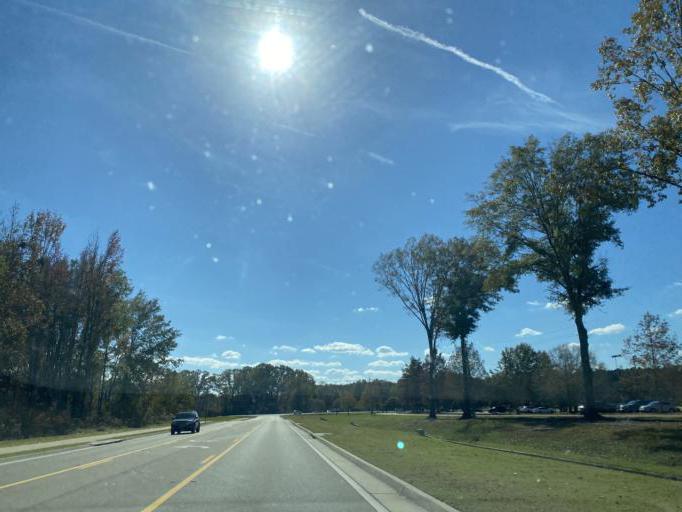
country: US
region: Mississippi
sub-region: Madison County
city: Madison
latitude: 32.4607
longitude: -90.1276
